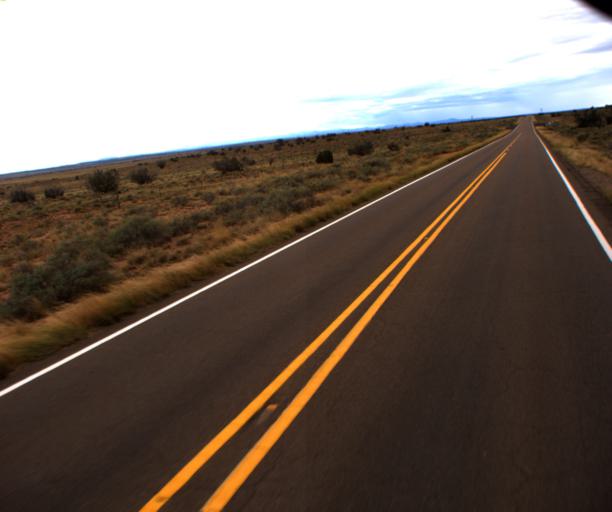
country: US
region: Arizona
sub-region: Navajo County
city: Snowflake
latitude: 34.6748
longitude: -110.1028
